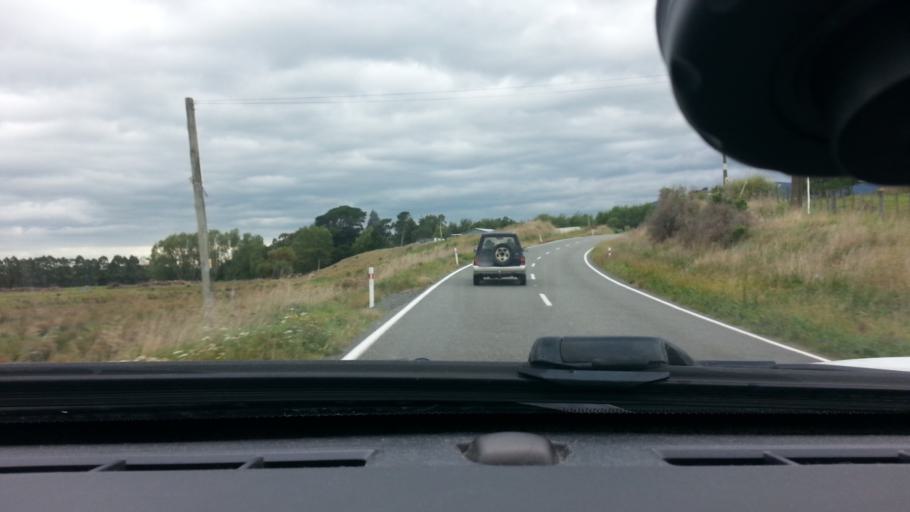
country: NZ
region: Wellington
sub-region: Upper Hutt City
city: Upper Hutt
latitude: -41.3270
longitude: 175.2255
